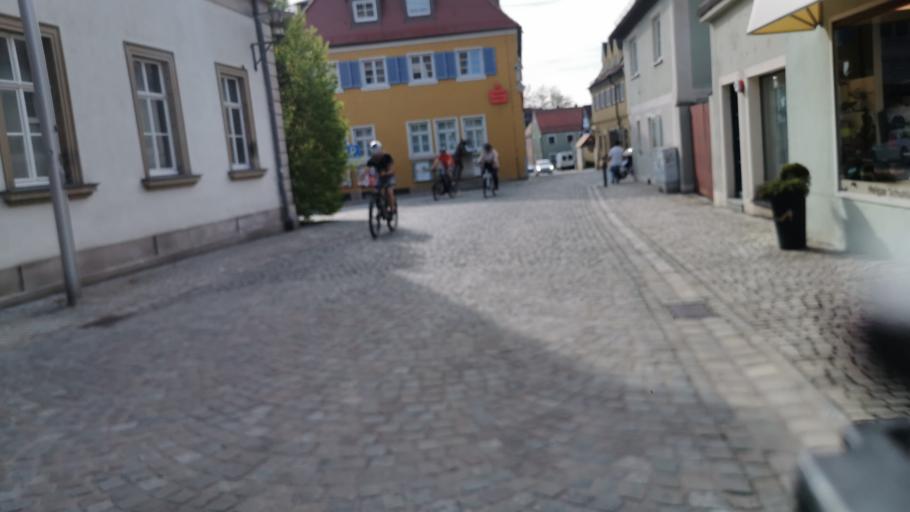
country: DE
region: Bavaria
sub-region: Regierungsbezirk Mittelfranken
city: Hochstadt an der Aisch
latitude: 49.7031
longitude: 10.8051
